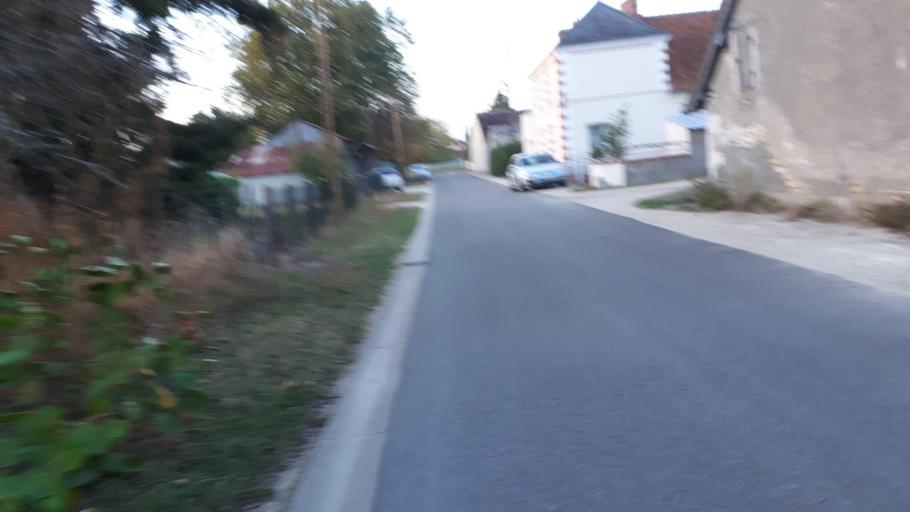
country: FR
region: Centre
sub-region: Departement du Loir-et-Cher
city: Saint-Romain-sur-Cher
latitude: 47.3634
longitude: 1.4068
